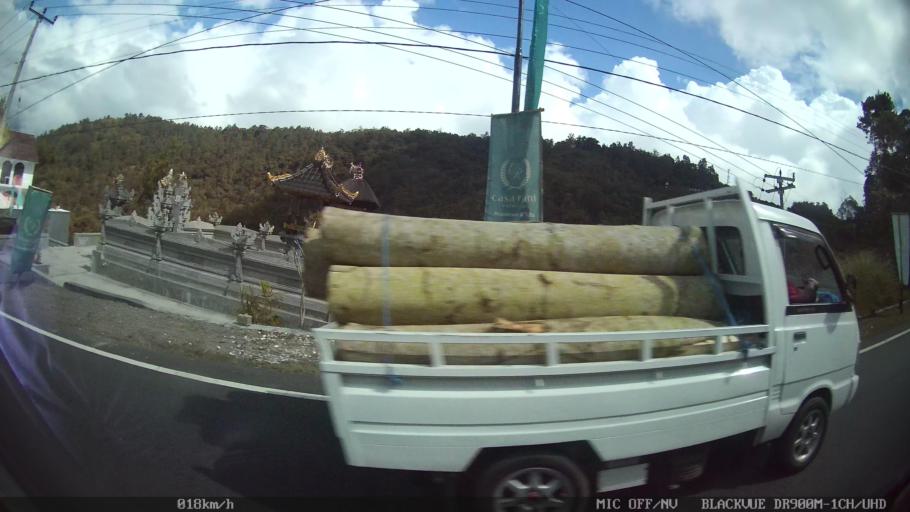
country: ID
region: Bali
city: Banjar Kedisan
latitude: -8.2800
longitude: 115.3691
